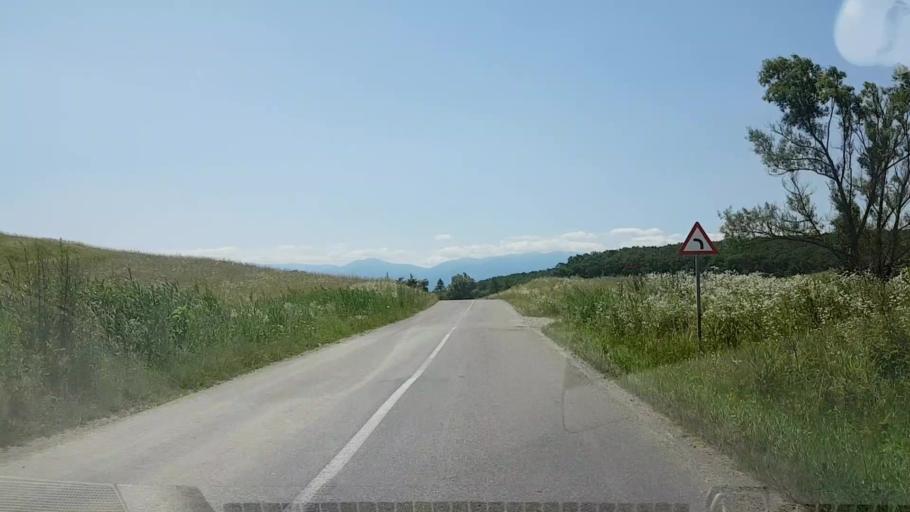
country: RO
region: Brasov
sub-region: Comuna Cincu
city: Cincu
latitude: 45.8901
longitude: 24.8118
